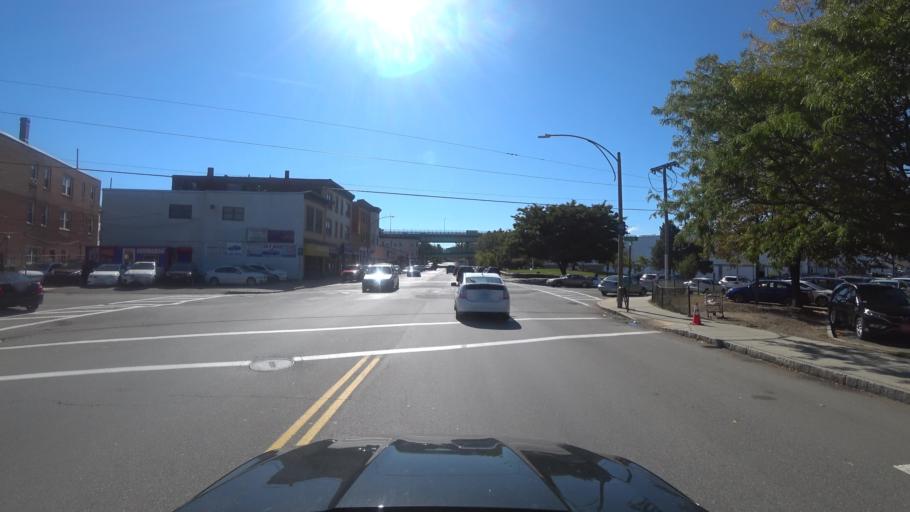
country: US
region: Massachusetts
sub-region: Suffolk County
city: Chelsea
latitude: 42.3936
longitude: -71.0392
